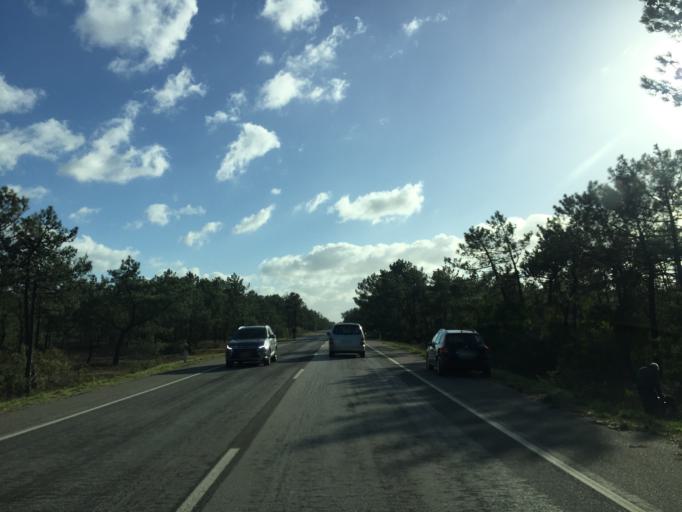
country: PT
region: Coimbra
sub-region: Figueira da Foz
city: Lavos
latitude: 40.0710
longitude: -8.8649
